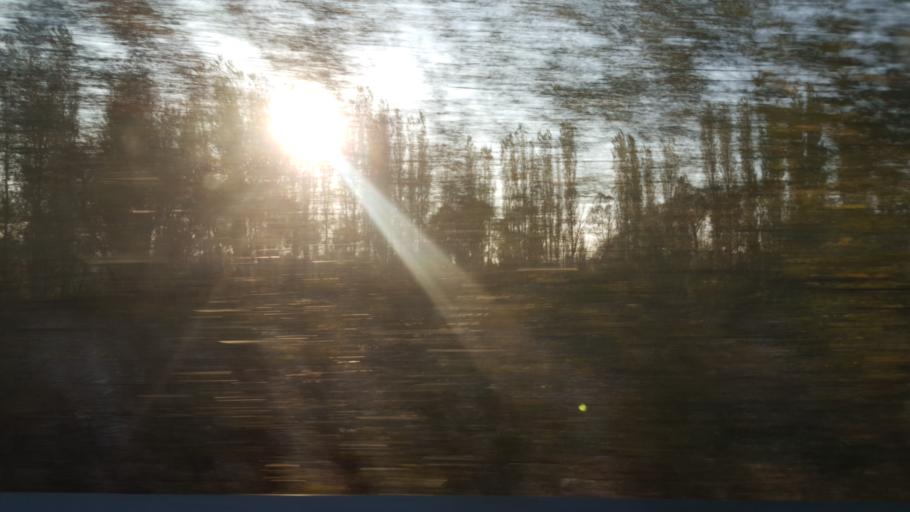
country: TR
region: Eskisehir
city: Mahmudiye
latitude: 39.5736
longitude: 30.9116
